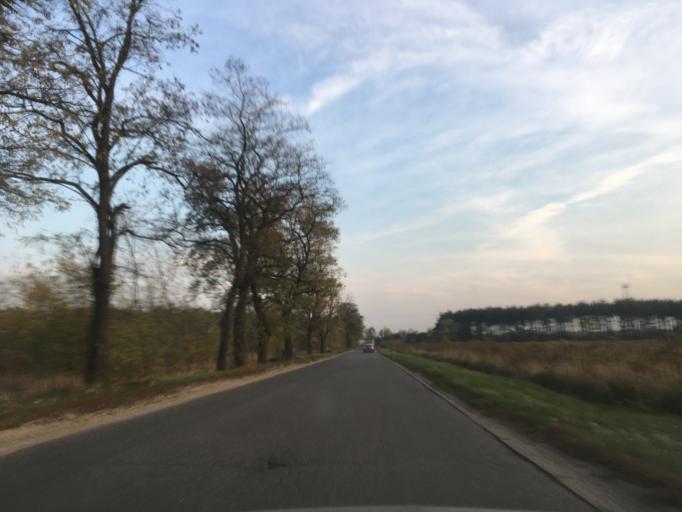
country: PL
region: Masovian Voivodeship
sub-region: Powiat piaseczynski
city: Lesznowola
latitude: 52.0655
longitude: 20.8974
